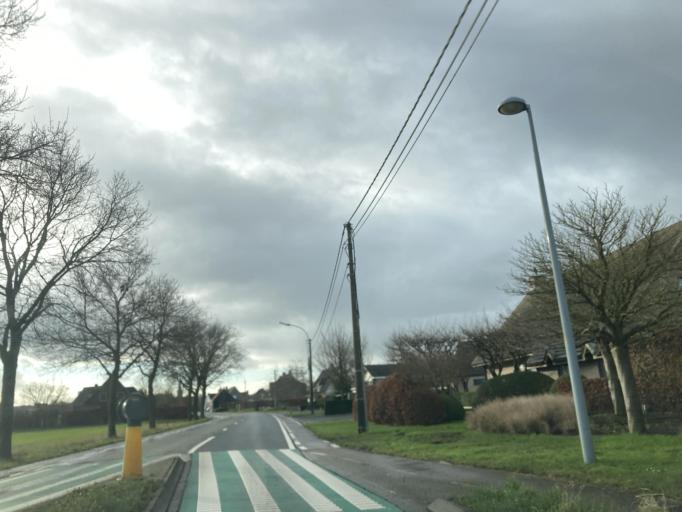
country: BE
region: Flanders
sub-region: Provincie West-Vlaanderen
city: Tielt
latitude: 51.0100
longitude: 3.3277
